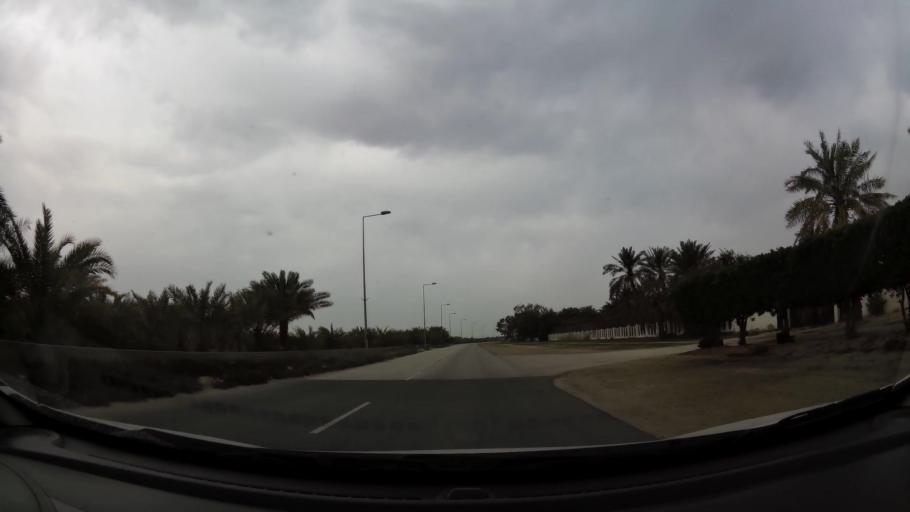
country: BH
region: Central Governorate
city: Dar Kulayb
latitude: 26.0295
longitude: 50.4825
